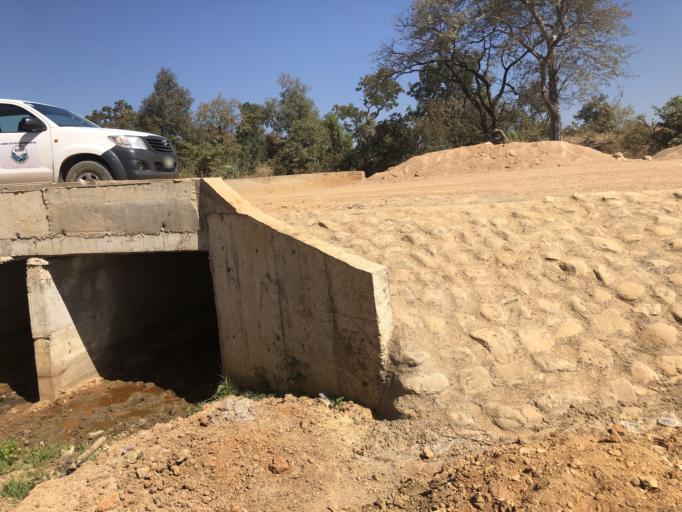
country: NG
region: Adamawa
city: Toungo
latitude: 8.1464
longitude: 11.9614
